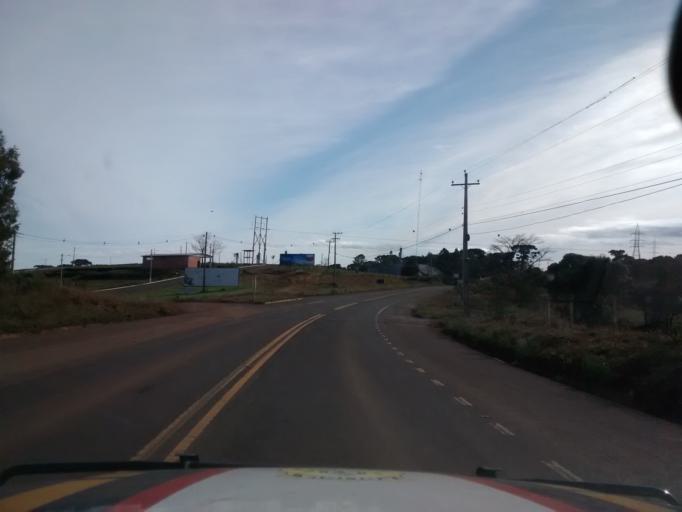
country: BR
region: Rio Grande do Sul
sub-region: Lagoa Vermelha
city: Lagoa Vermelha
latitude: -28.1913
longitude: -51.5260
